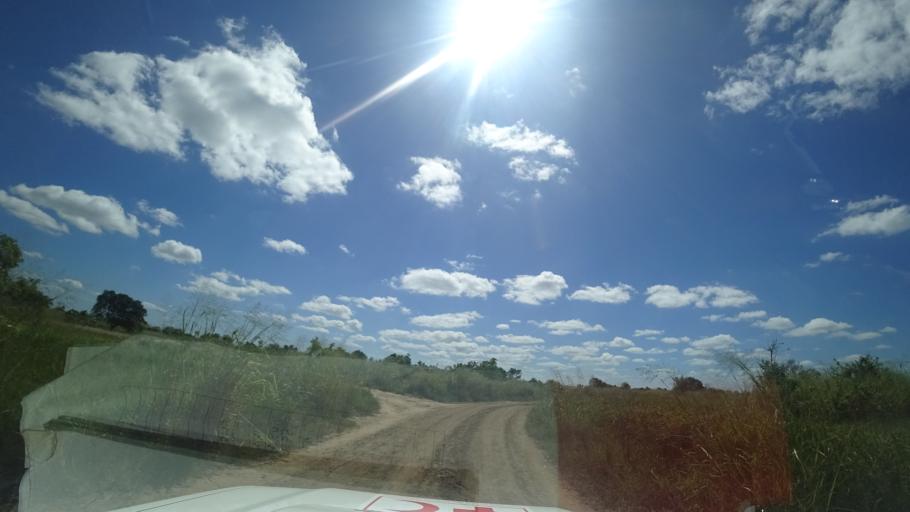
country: MZ
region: Sofala
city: Dondo
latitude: -19.4614
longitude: 34.5943
